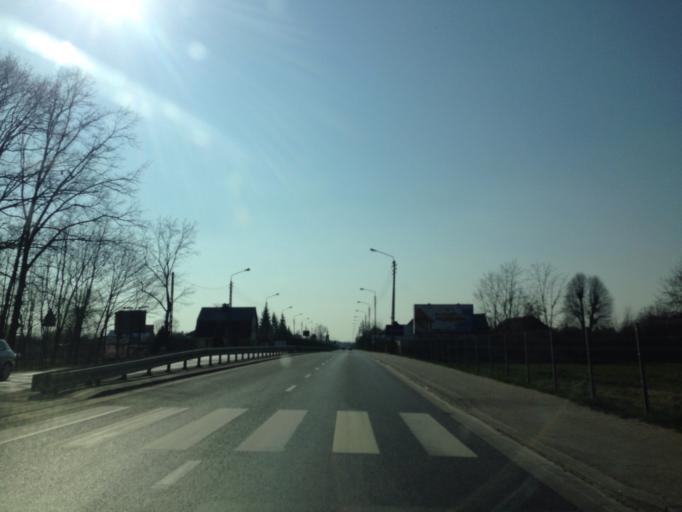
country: PL
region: Lower Silesian Voivodeship
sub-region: Powiat wroclawski
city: Dlugoleka
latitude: 51.1925
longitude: 17.2486
